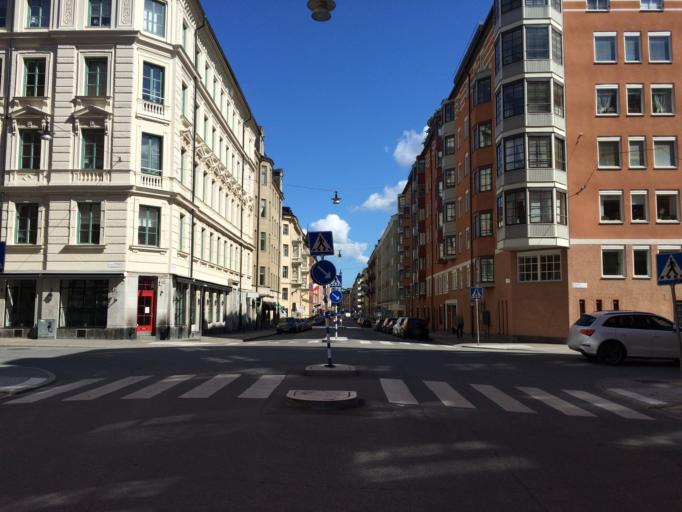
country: SE
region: Stockholm
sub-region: Stockholms Kommun
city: OEstermalm
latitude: 59.3392
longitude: 18.0768
